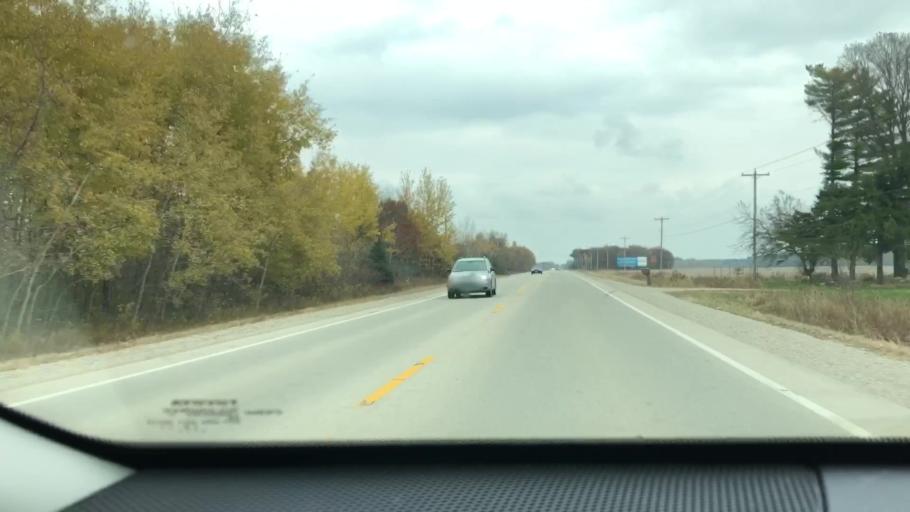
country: US
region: Wisconsin
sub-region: Brown County
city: Oneida
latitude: 44.5021
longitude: -88.2239
